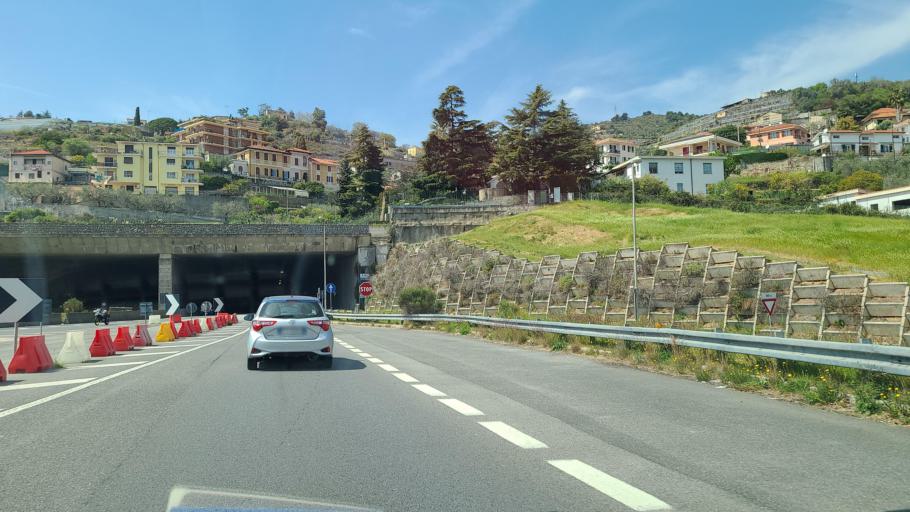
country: IT
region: Liguria
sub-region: Provincia di Imperia
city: San Remo
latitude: 43.8303
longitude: 7.7961
